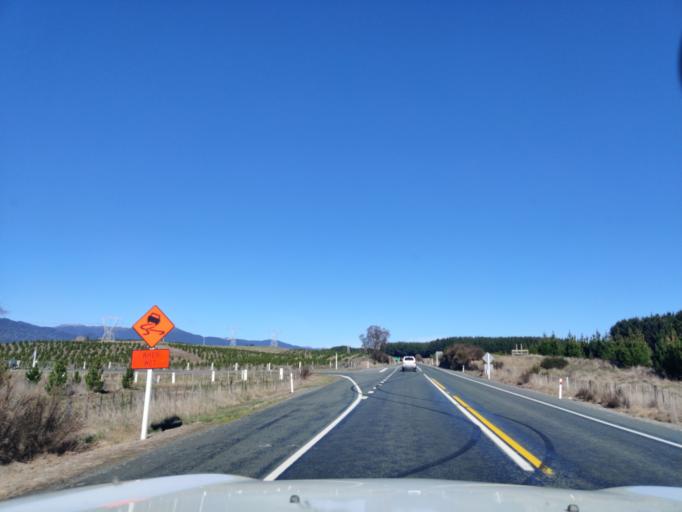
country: NZ
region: Waikato
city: Turangi
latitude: -39.0778
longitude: 175.8085
